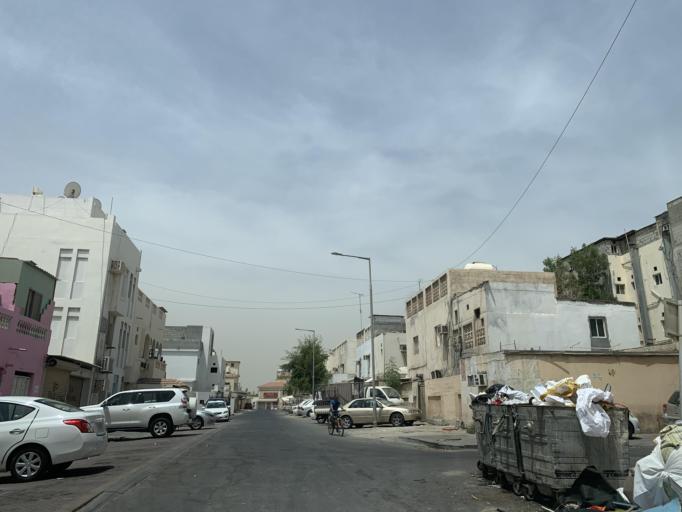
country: BH
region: Northern
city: Madinat `Isa
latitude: 26.1773
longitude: 50.5533
